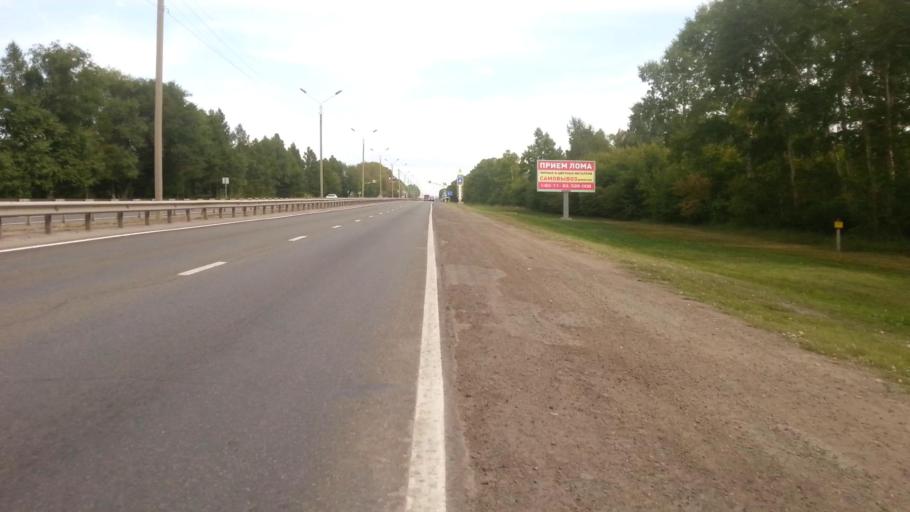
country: RU
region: Altai Krai
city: Vlasikha
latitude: 53.3529
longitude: 83.5634
